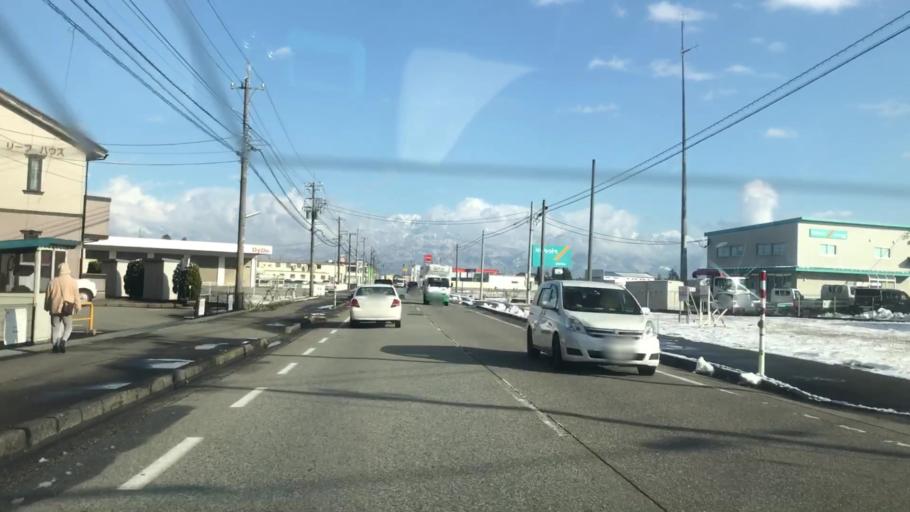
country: JP
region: Toyama
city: Toyama-shi
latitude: 36.6728
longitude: 137.2686
